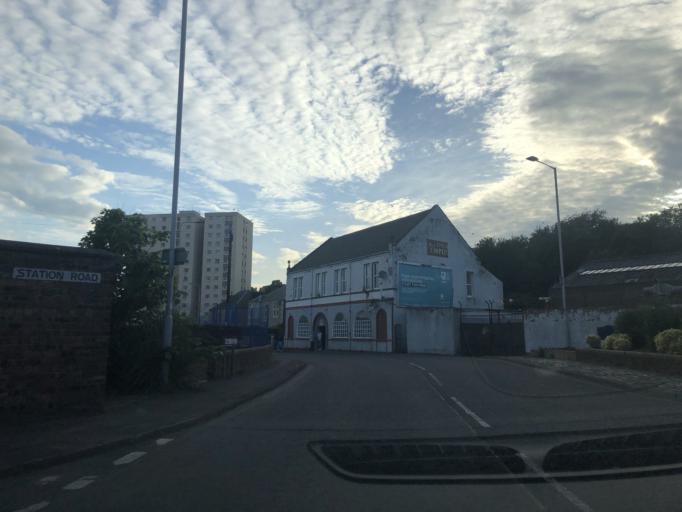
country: GB
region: Scotland
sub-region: Fife
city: Leven
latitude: 56.1835
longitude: -3.0132
